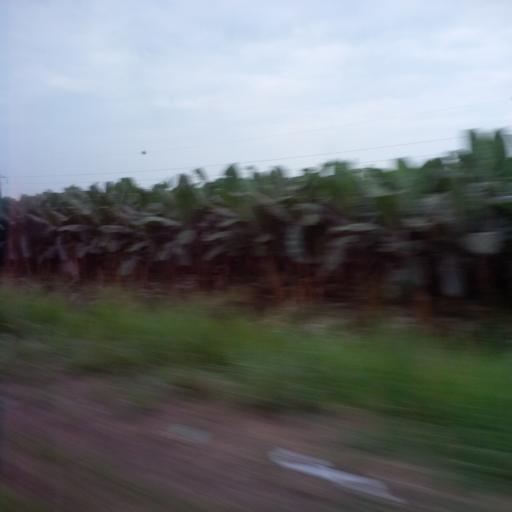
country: EC
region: Canar
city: La Troncal
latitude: -2.3453
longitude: -79.3677
